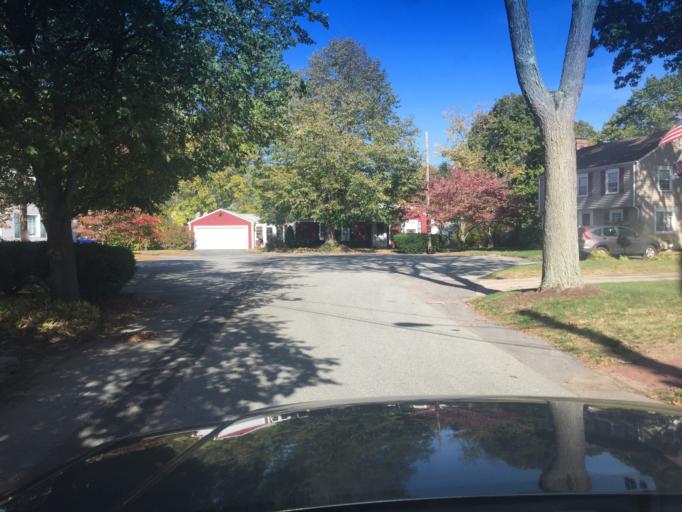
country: US
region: Rhode Island
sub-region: Providence County
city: East Providence
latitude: 41.8327
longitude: -71.3632
